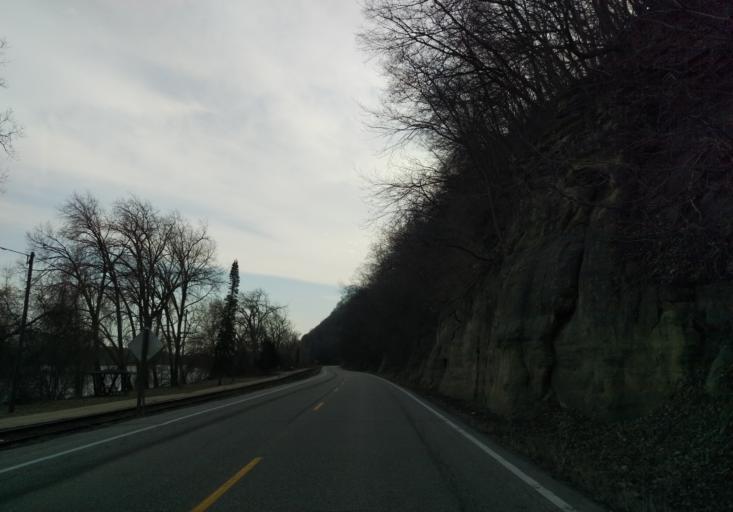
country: US
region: Wisconsin
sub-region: Crawford County
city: Prairie du Chien
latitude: 43.0701
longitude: -91.1804
